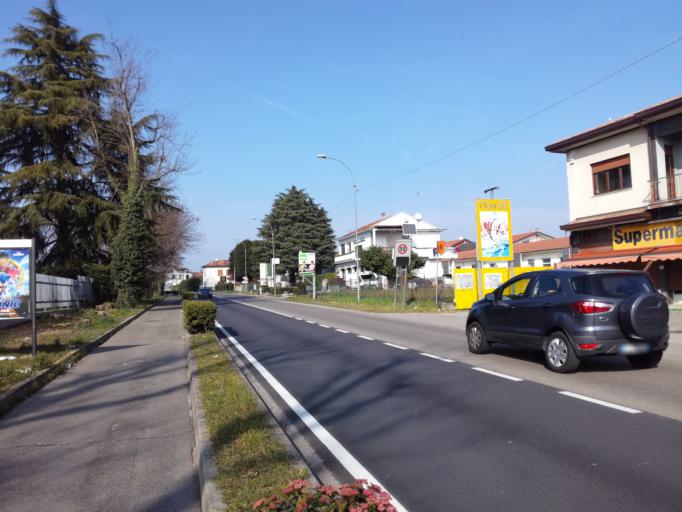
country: IT
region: Lombardy
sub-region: Provincia di Monza e Brianza
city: Lentate sul Seveso
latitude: 45.6868
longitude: 9.1100
